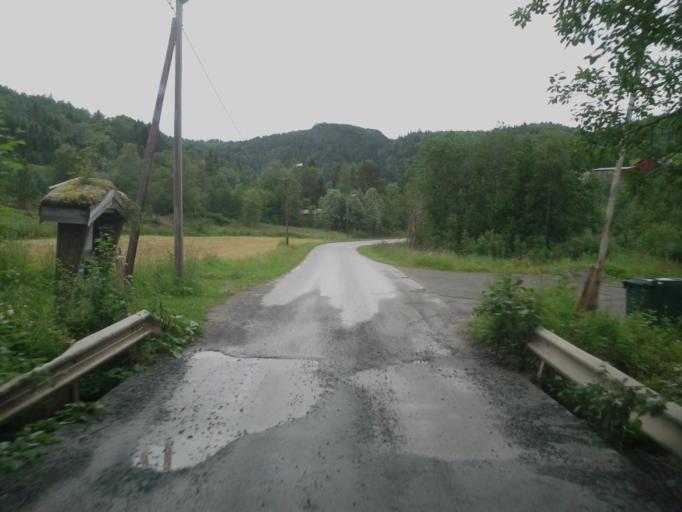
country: NO
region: Sor-Trondelag
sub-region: Melhus
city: Lundamo
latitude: 63.1367
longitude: 10.3267
